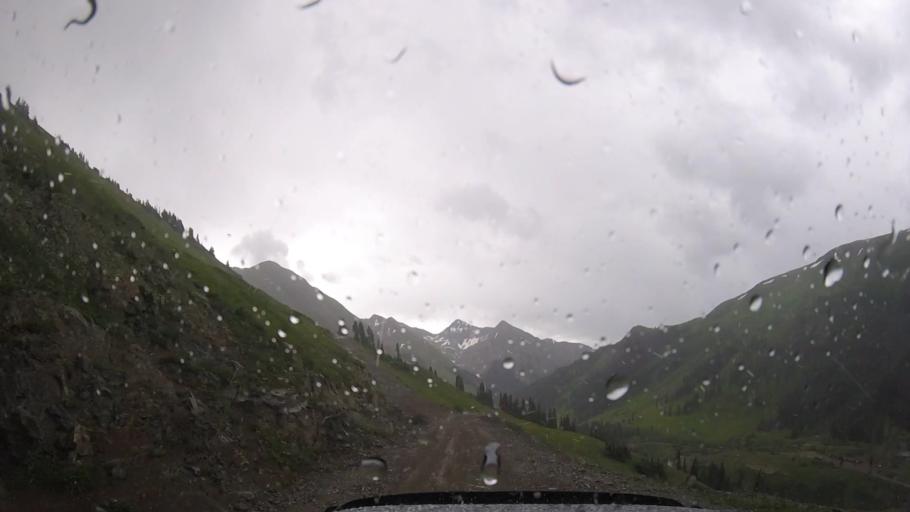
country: US
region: Colorado
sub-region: Ouray County
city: Ouray
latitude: 37.9342
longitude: -107.5689
